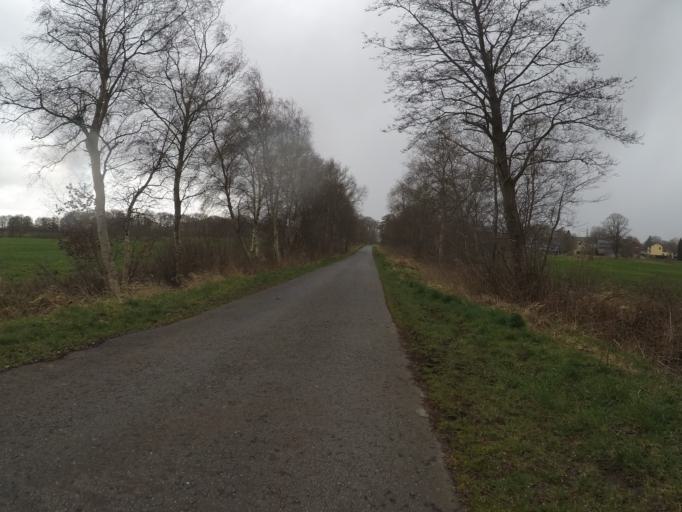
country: DE
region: Lower Saxony
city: Langen
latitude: 53.6163
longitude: 8.6387
